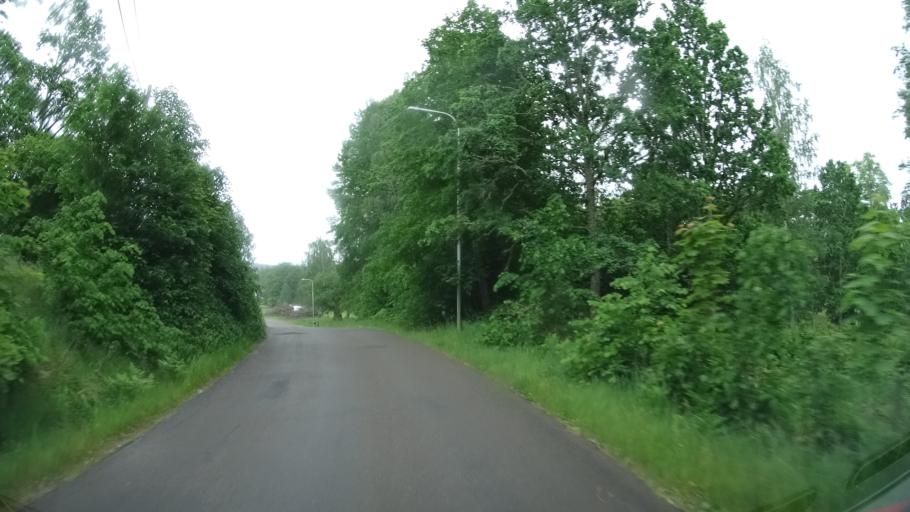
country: SE
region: Joenkoeping
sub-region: Eksjo Kommun
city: Mariannelund
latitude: 57.6784
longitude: 15.5817
